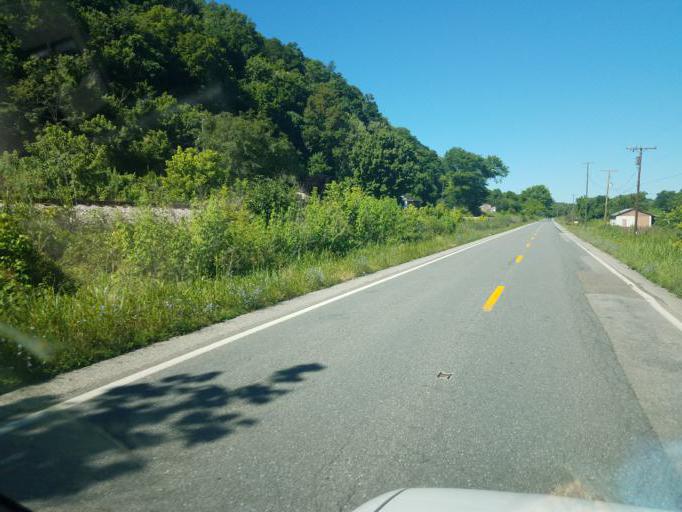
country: US
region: West Virginia
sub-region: Cabell County
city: Lesage
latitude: 38.5896
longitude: -82.1949
